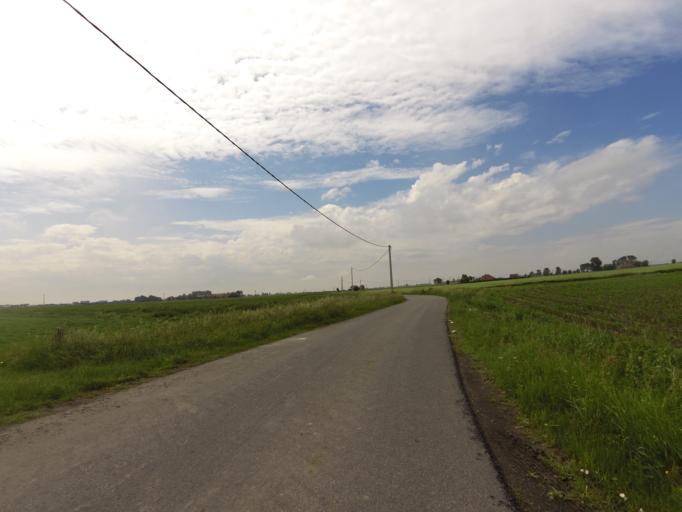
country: BE
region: Flanders
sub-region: Provincie West-Vlaanderen
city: Middelkerke
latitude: 51.1481
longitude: 2.8420
